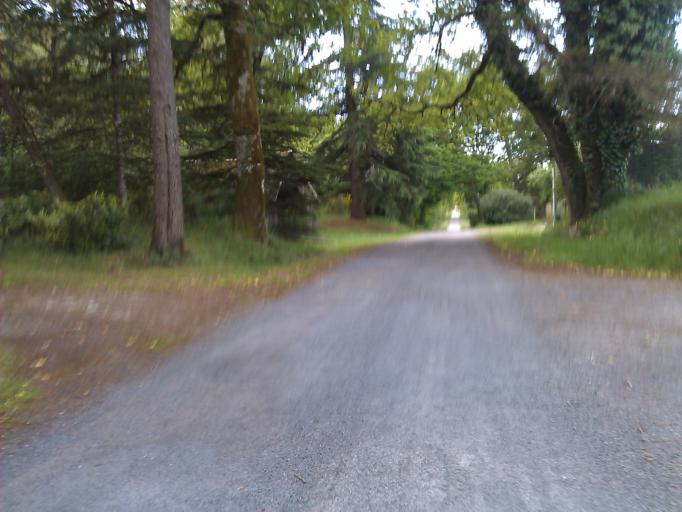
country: FR
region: Poitou-Charentes
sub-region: Departement de la Charente-Maritime
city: Clerac
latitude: 45.1642
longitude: -0.2699
